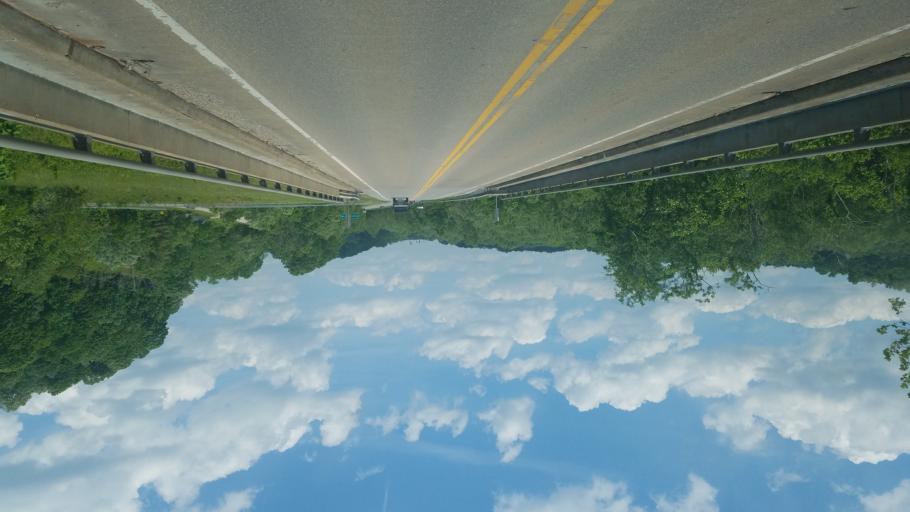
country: US
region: Ohio
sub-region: Meigs County
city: Middleport
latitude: 38.9961
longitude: -82.0763
